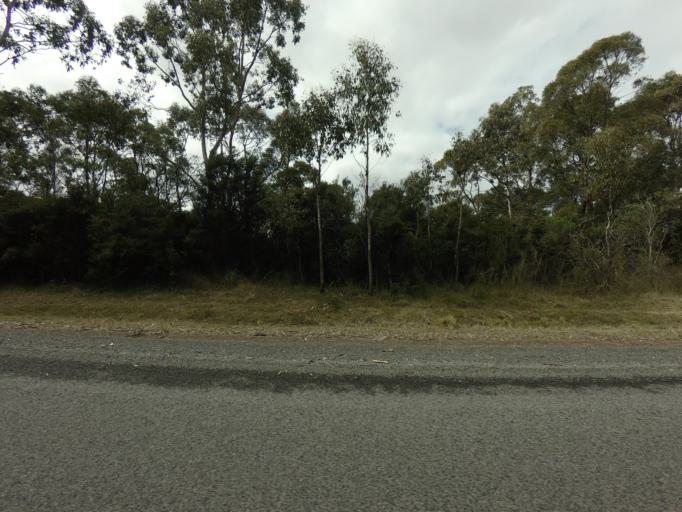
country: AU
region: Tasmania
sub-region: Huon Valley
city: Geeveston
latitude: -43.4389
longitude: 146.9042
